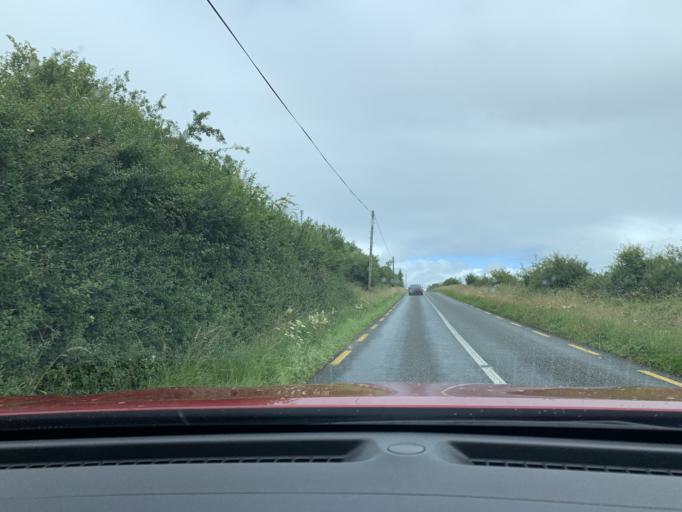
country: IE
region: Connaught
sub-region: County Leitrim
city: Carrick-on-Shannon
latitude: 53.8842
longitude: -8.1529
